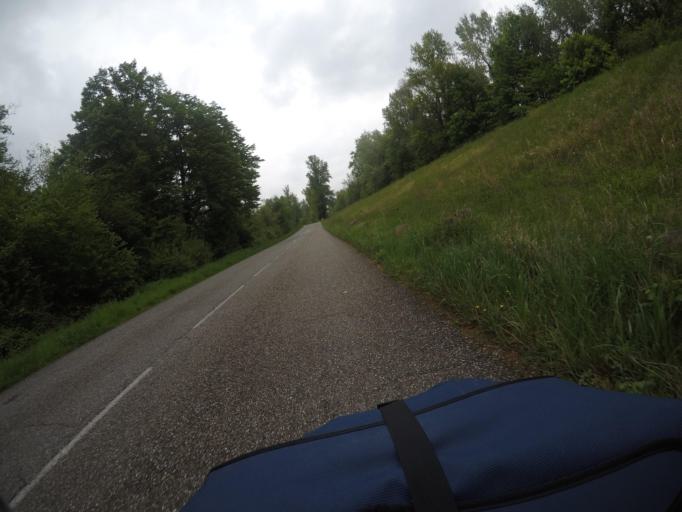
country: DE
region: Baden-Wuerttemberg
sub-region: Karlsruhe Region
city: Hugelsheim
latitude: 48.8391
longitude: 8.1035
